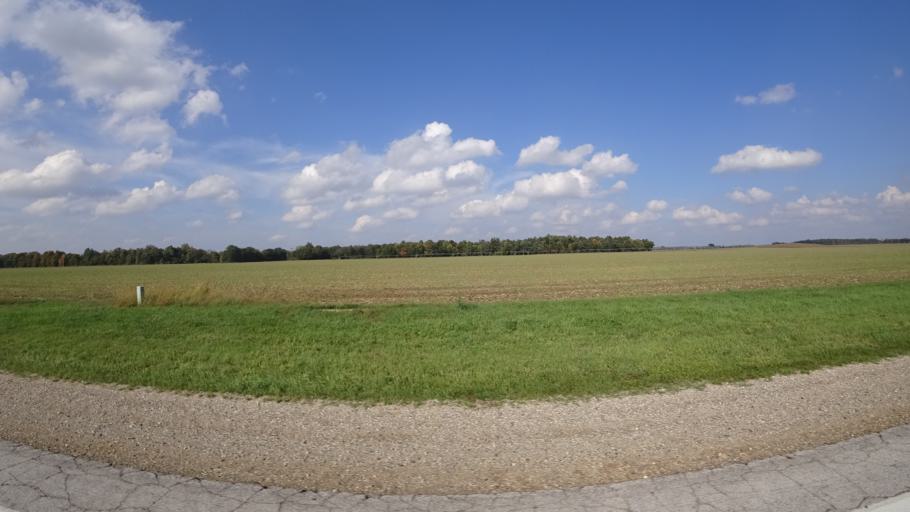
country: US
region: Michigan
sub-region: Saint Joseph County
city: Colon
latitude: 42.0101
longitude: -85.3746
